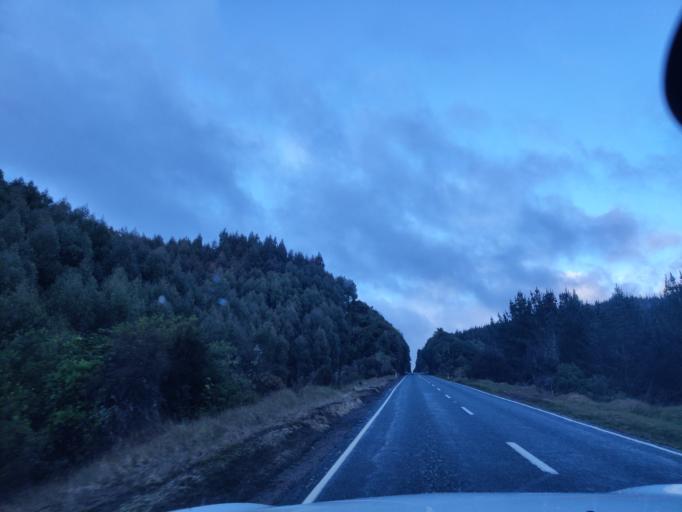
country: NZ
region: Waikato
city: Turangi
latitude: -38.7043
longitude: 175.6780
